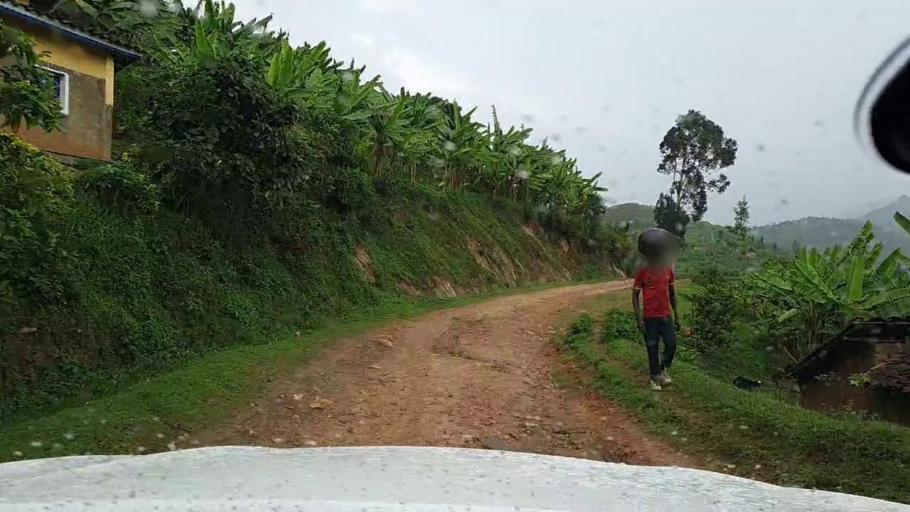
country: RW
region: Western Province
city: Kibuye
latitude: -2.0780
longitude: 29.4484
